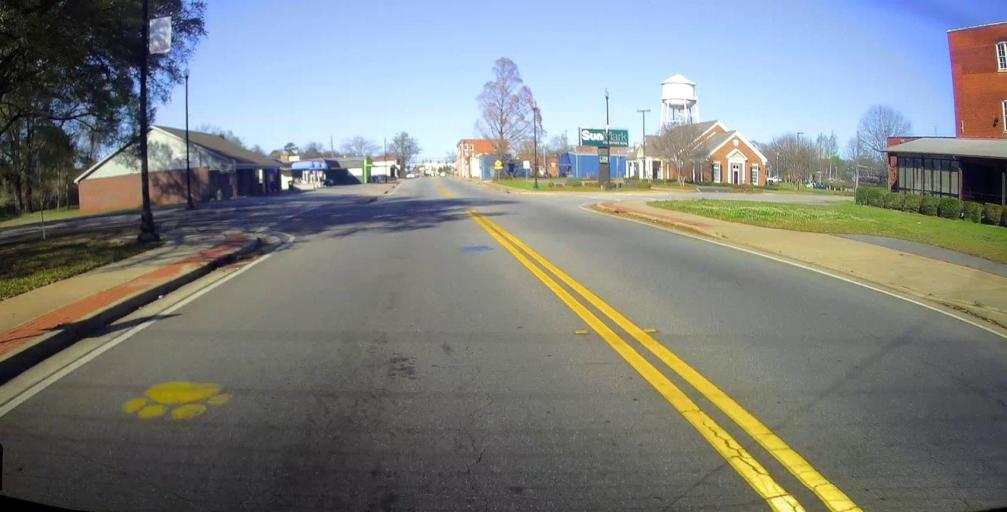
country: US
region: Georgia
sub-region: Peach County
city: Fort Valley
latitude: 32.5513
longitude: -83.8882
